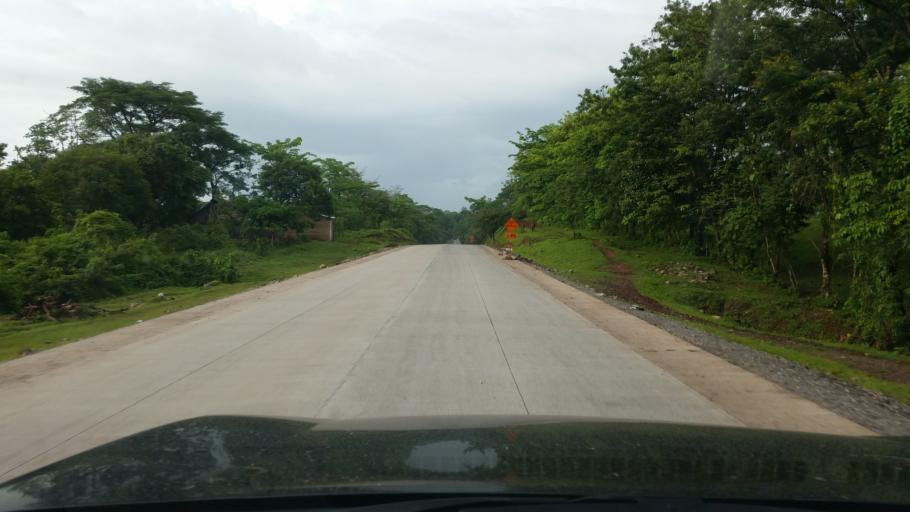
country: NI
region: Matagalpa
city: Rio Blanco
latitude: 13.1136
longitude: -85.0630
